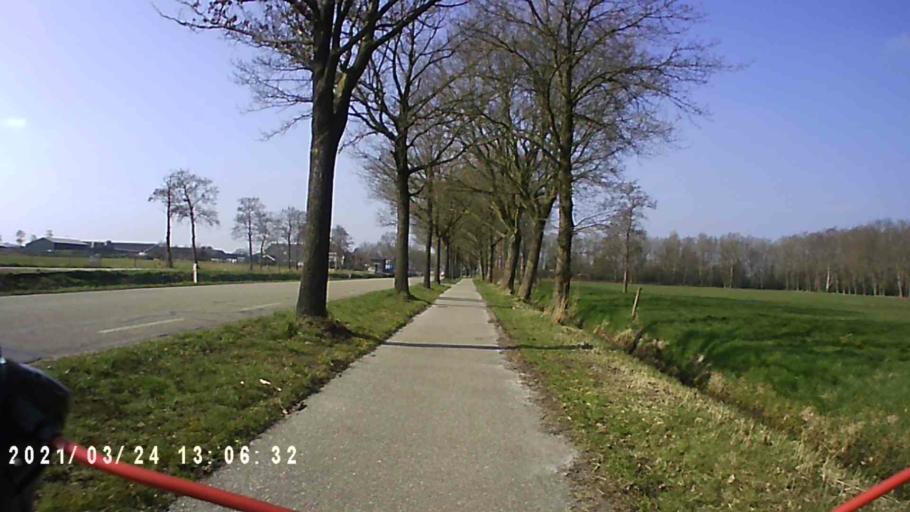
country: NL
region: Groningen
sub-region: Gemeente Leek
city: Leek
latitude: 53.1301
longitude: 6.3062
